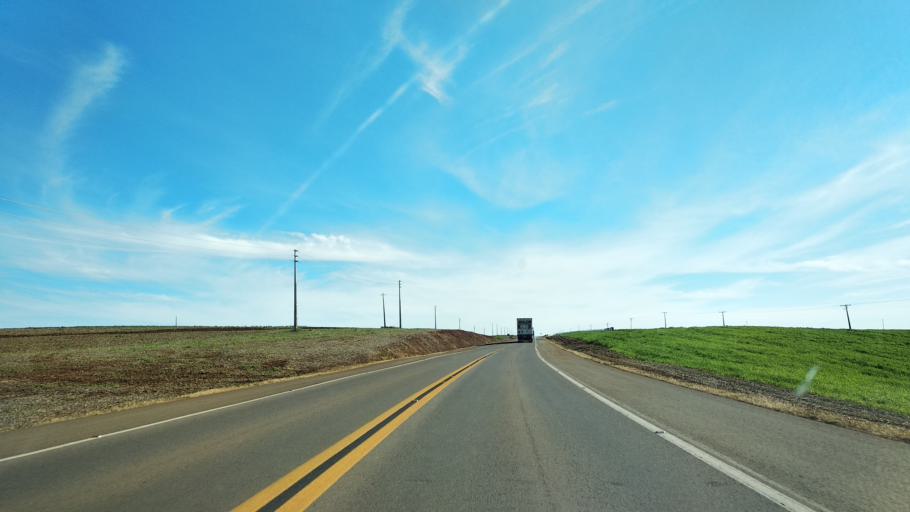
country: BR
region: Santa Catarina
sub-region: Campos Novos
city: Campos Novos
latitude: -27.4859
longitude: -51.3176
